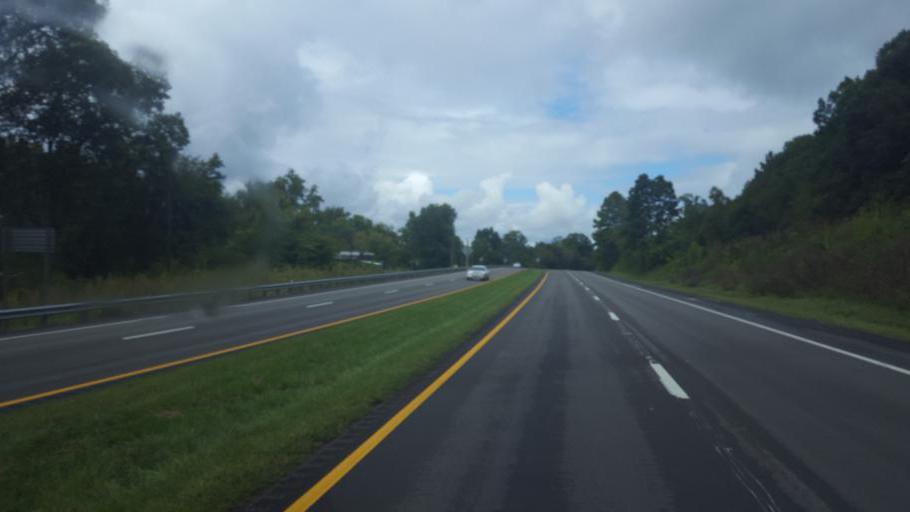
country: US
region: Ohio
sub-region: Scioto County
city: Lucasville
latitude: 38.8422
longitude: -82.9847
